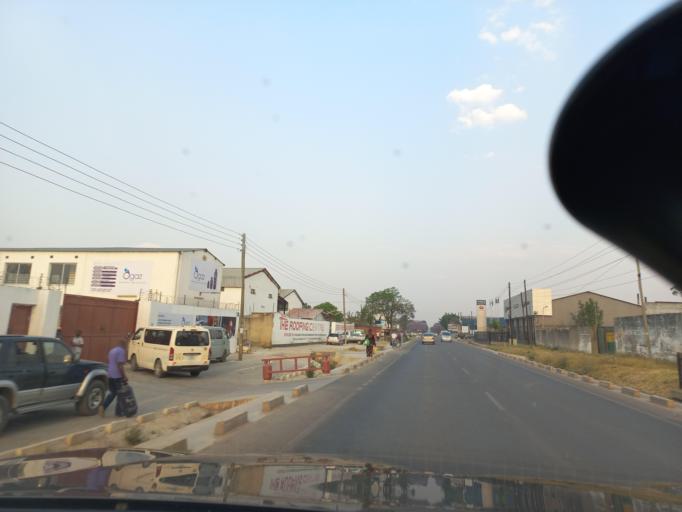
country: ZM
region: Lusaka
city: Lusaka
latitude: -15.3937
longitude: 28.2709
